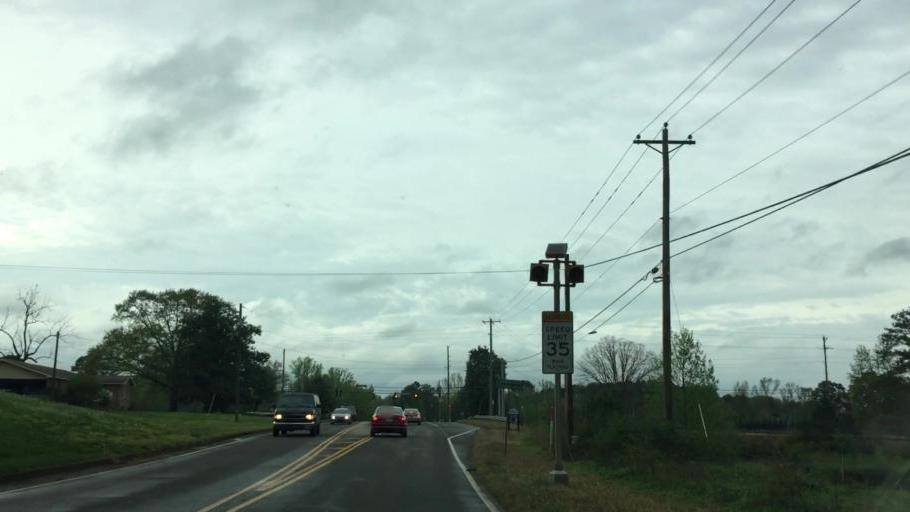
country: US
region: Georgia
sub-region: Cherokee County
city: Canton
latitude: 34.2110
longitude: -84.3958
